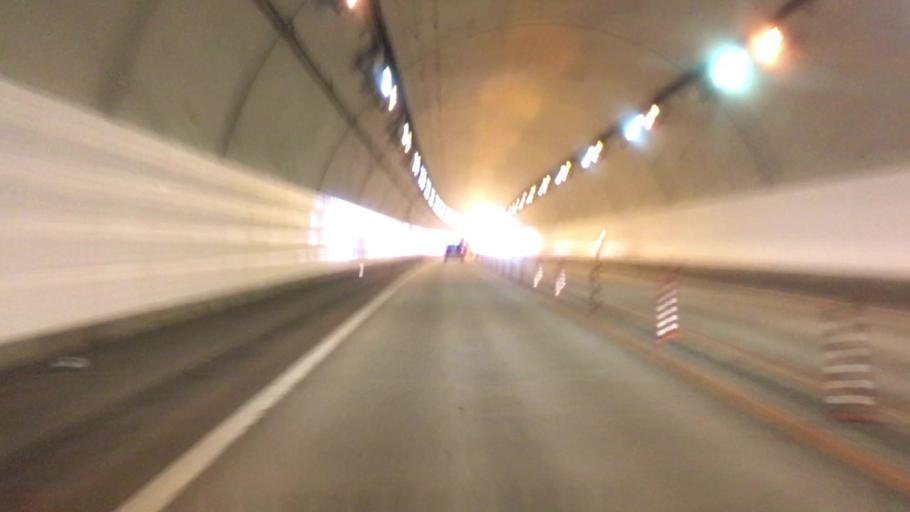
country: JP
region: Kyoto
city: Fukuchiyama
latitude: 35.2773
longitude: 134.9900
